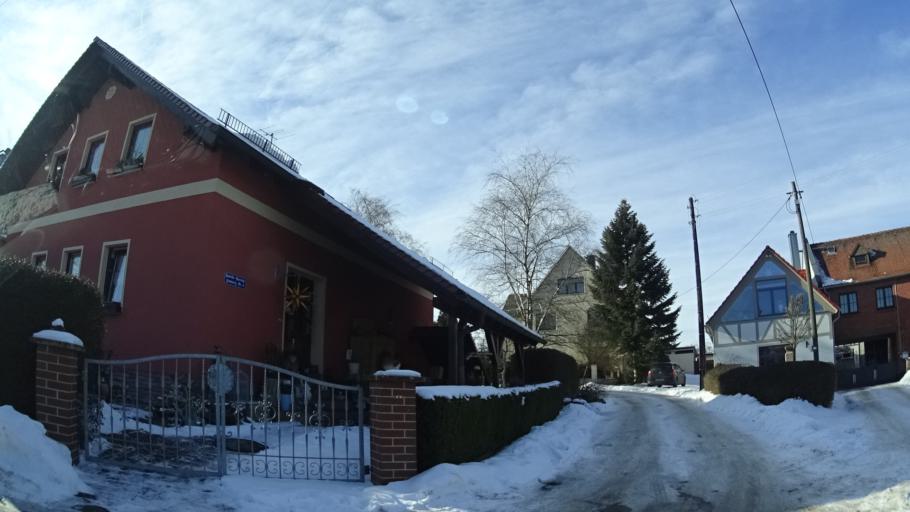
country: DE
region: Thuringia
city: Bucha
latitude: 50.8570
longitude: 11.4988
